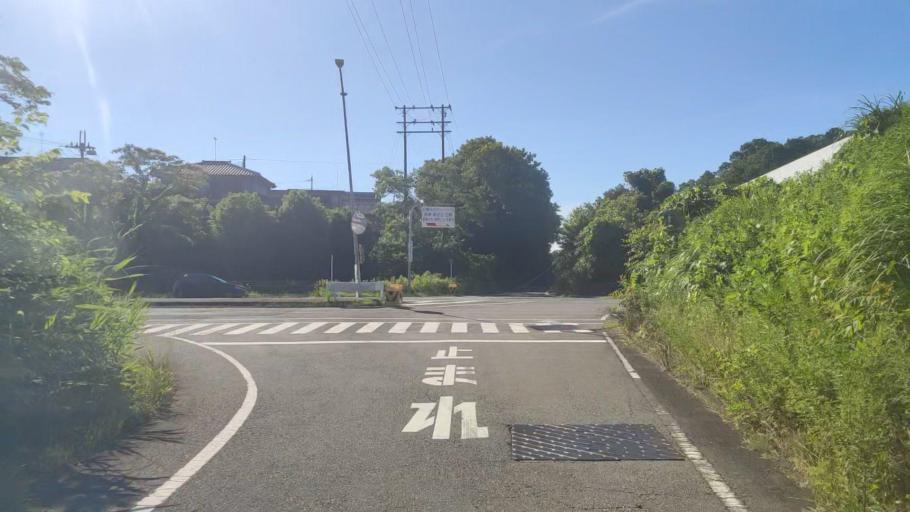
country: JP
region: Shiga Prefecture
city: Minakuchicho-matoba
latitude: 34.9735
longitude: 136.1884
